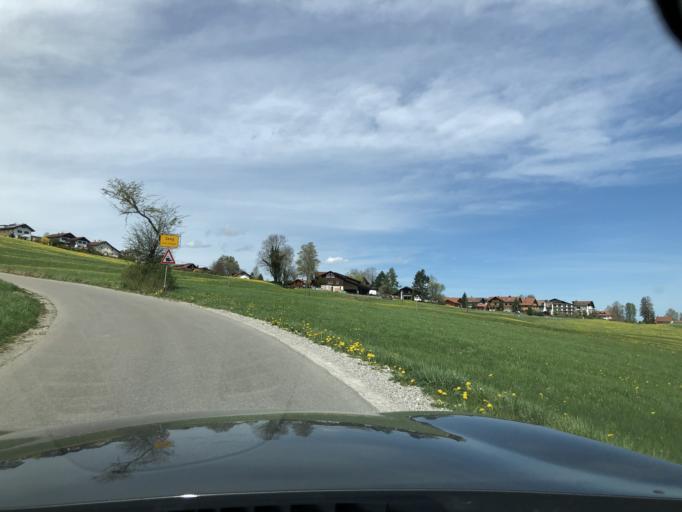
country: DE
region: Bavaria
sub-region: Swabia
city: Seeg
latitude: 47.6488
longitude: 10.6154
